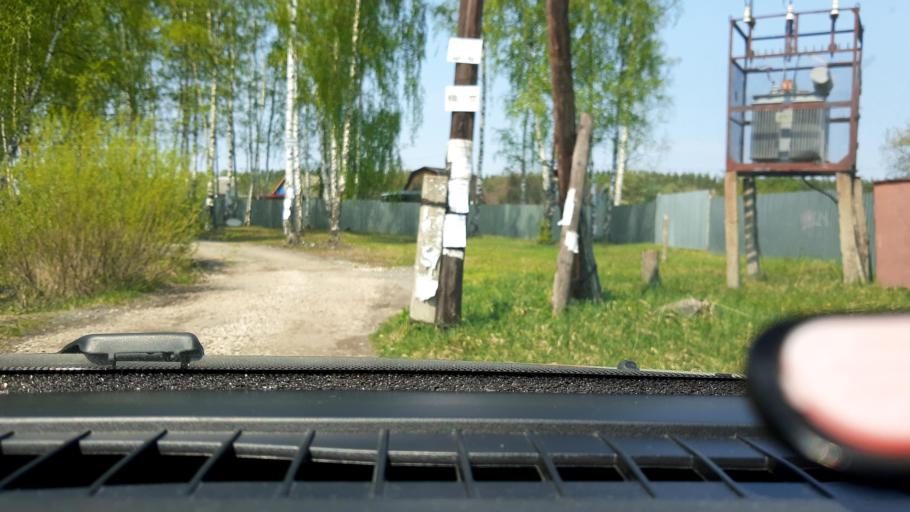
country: RU
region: Nizjnij Novgorod
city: Gorbatovka
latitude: 56.2719
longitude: 43.7973
